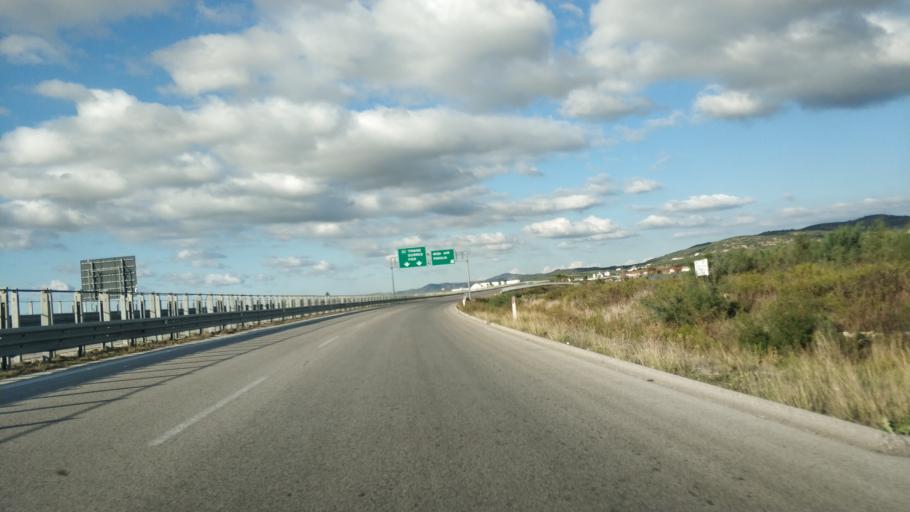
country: AL
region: Vlore
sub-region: Rrethi i Vlores
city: Novosele
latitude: 40.5524
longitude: 19.4597
